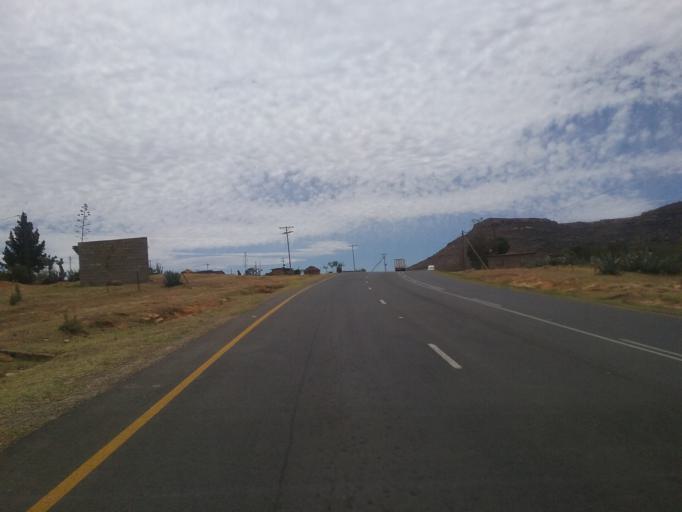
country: LS
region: Mafeteng
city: Mafeteng
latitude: -29.6460
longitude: 27.4657
